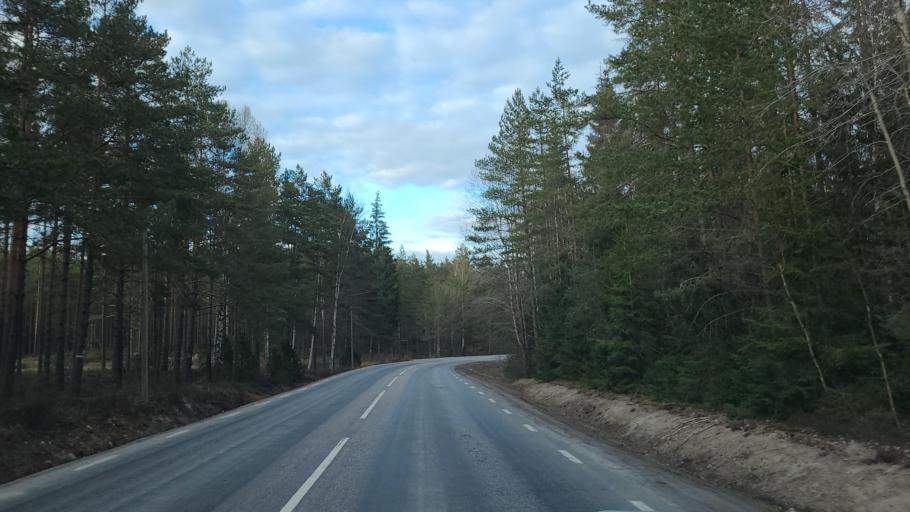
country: SE
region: Soedermanland
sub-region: Nykopings Kommun
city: Olstorp
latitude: 58.7288
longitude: 16.6919
